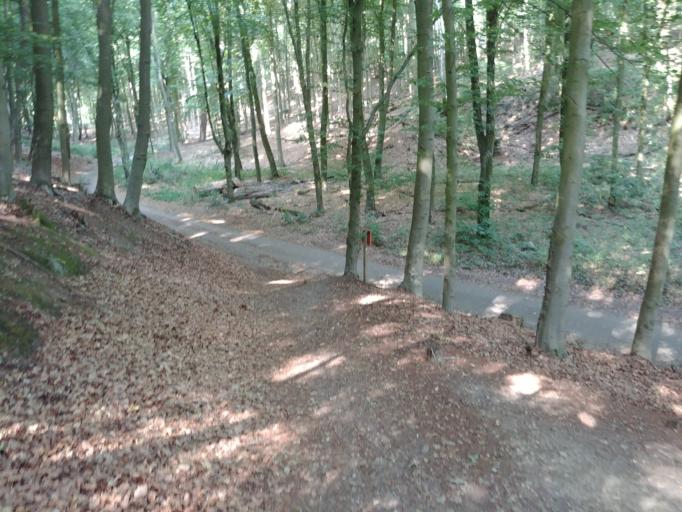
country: NL
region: Gelderland
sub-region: Gemeente Renkum
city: Doorwerth
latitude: 51.9692
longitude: 5.7932
